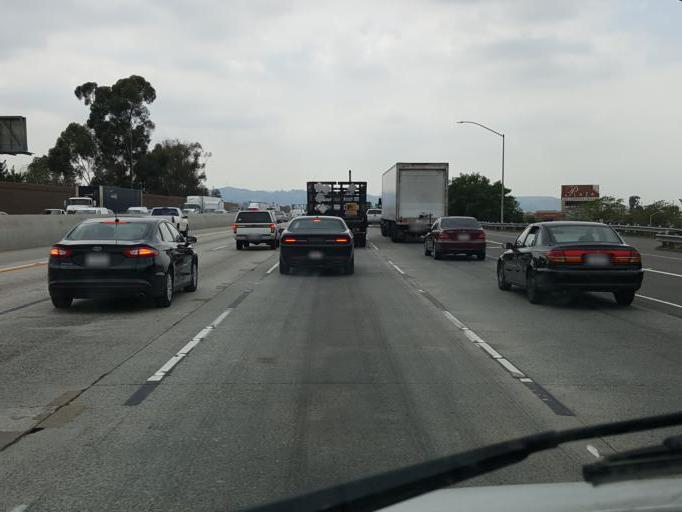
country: US
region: California
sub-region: Los Angeles County
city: Rowland Heights
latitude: 33.9944
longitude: -117.9093
